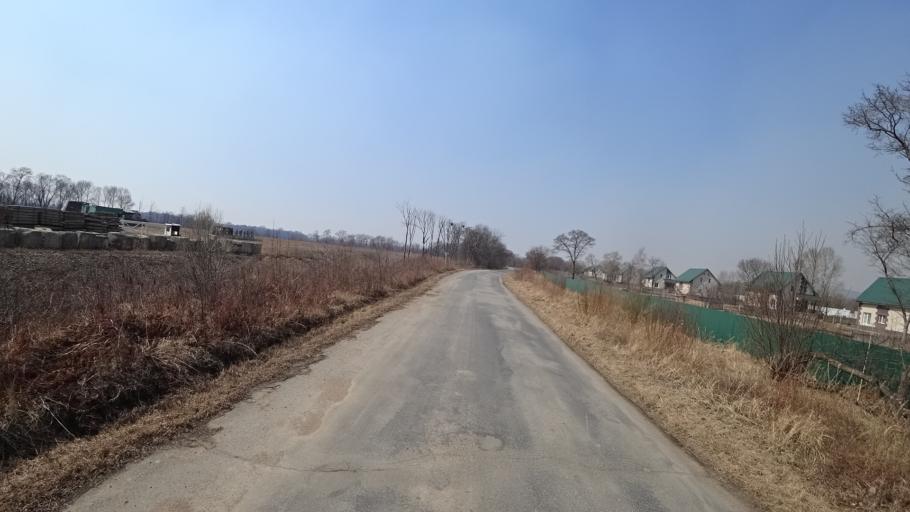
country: RU
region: Amur
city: Novobureyskiy
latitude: 49.7853
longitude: 129.9198
